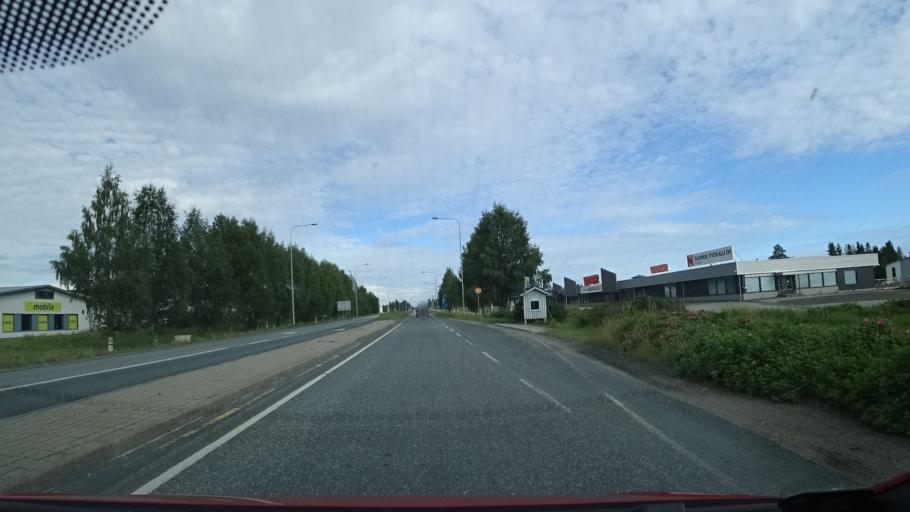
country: FI
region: Lapland
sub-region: Kemi-Tornio
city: Keminmaa
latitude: 65.7993
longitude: 24.5060
